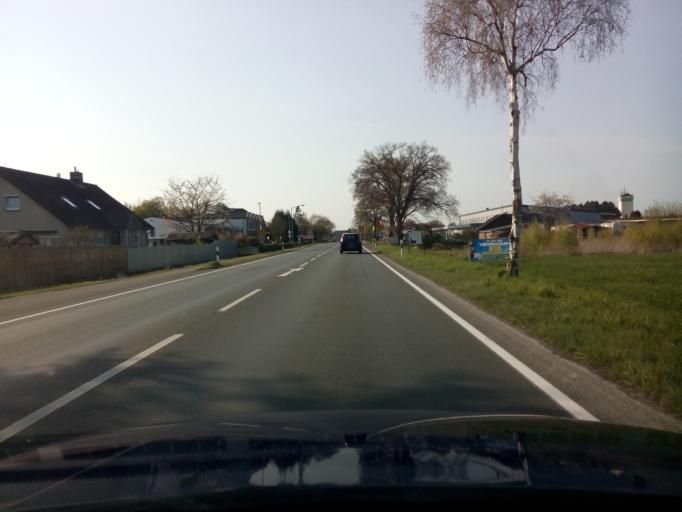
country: DE
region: Lower Saxony
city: Sustedt
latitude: 52.8726
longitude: 8.8689
